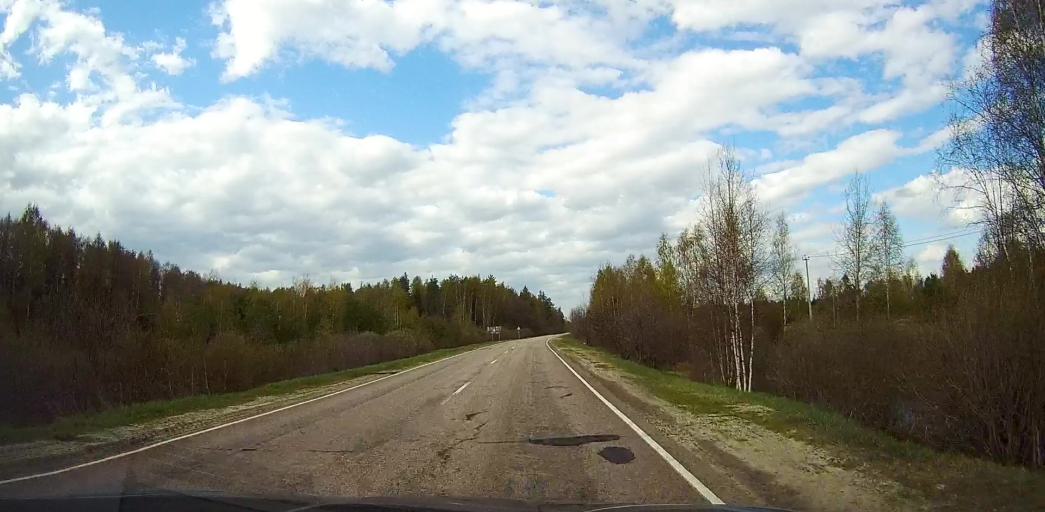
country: RU
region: Moskovskaya
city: Rakhmanovo
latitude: 55.6795
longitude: 38.6436
